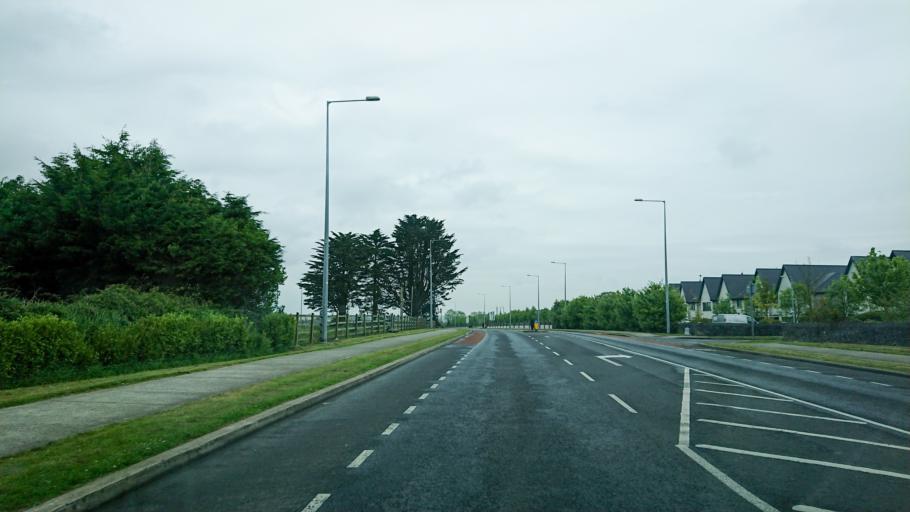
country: IE
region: Munster
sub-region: Waterford
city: Waterford
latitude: 52.2336
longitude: -7.1412
